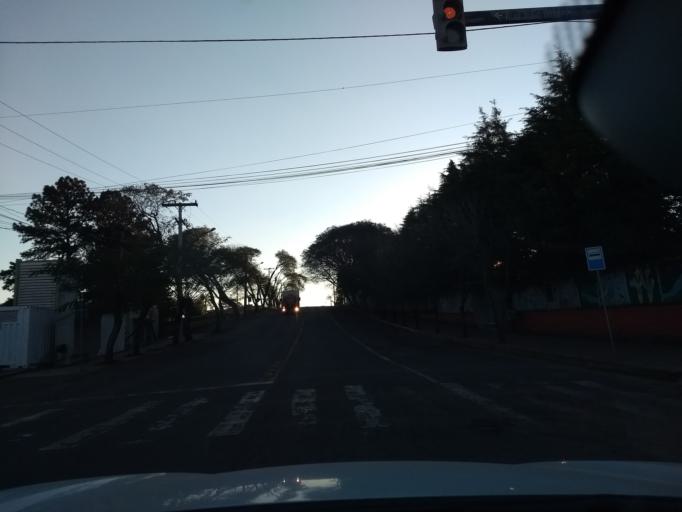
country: BR
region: Rio Grande do Sul
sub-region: Santa Cruz Do Sul
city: Santa Cruz do Sul
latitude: -29.7153
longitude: -52.5088
